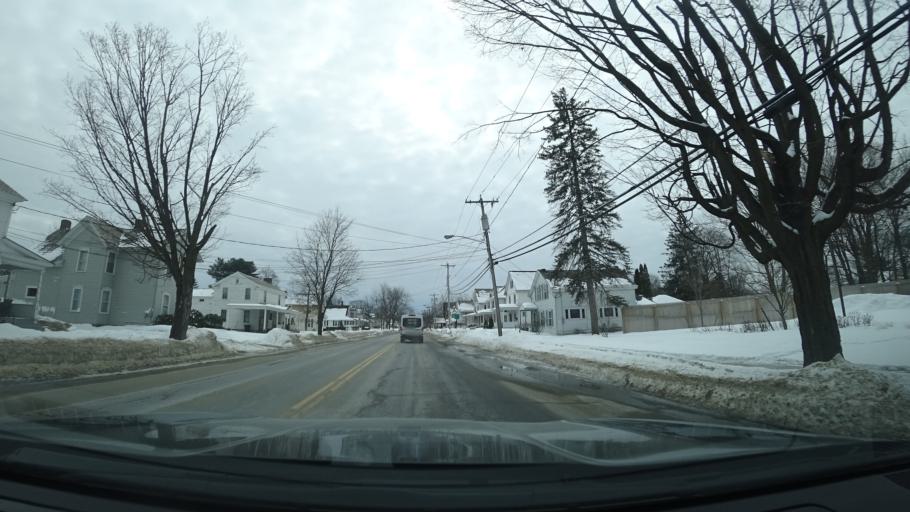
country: US
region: New York
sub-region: Saratoga County
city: South Glens Falls
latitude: 43.2986
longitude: -73.6348
